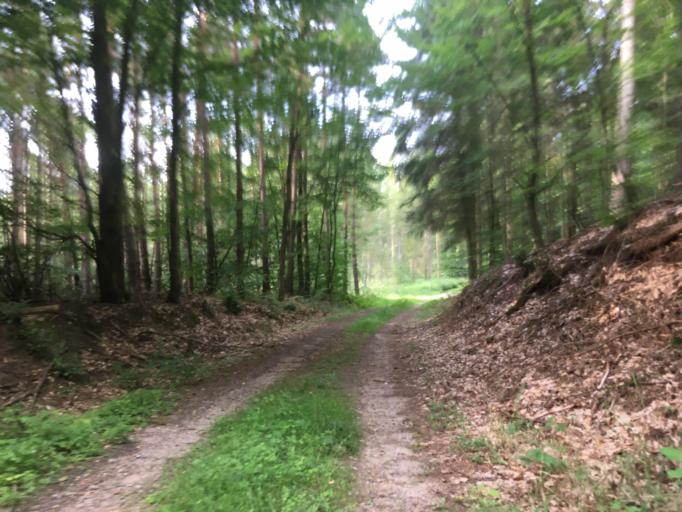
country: DE
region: Brandenburg
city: Eberswalde
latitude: 52.7995
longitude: 13.8197
